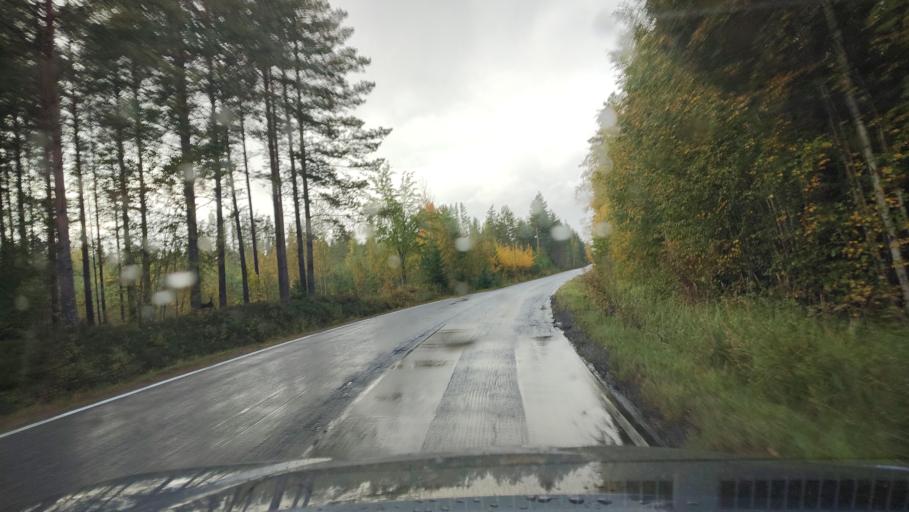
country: FI
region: Southern Ostrobothnia
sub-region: Suupohja
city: Karijoki
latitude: 62.3190
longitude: 21.6799
